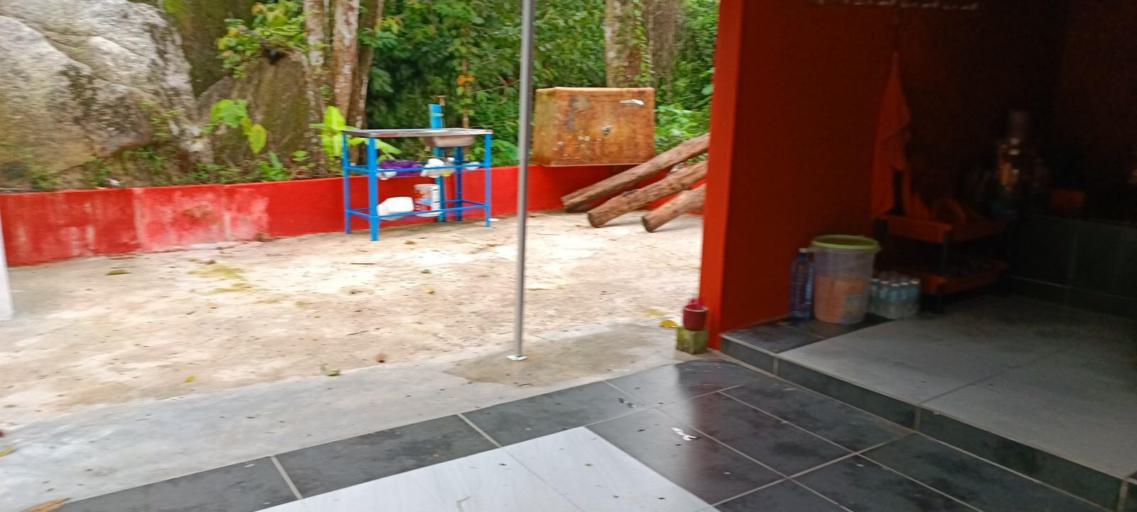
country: MY
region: Penang
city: Bukit Mertajam
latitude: 5.3722
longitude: 100.4801
